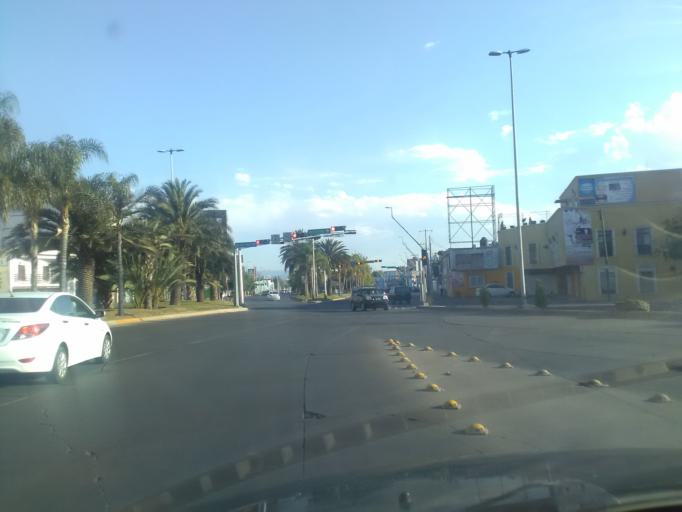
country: MX
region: Durango
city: Victoria de Durango
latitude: 24.0187
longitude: -104.6641
